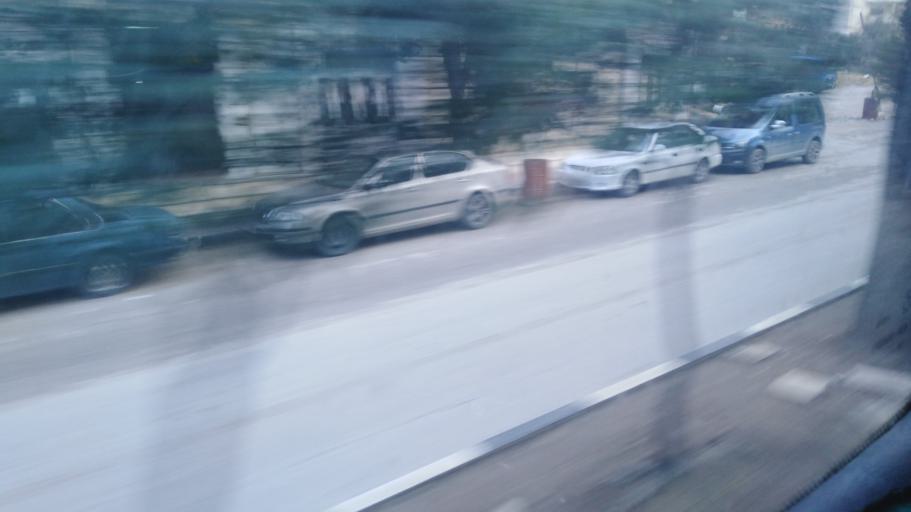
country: PS
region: West Bank
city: Hebron
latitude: 31.5296
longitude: 35.0940
